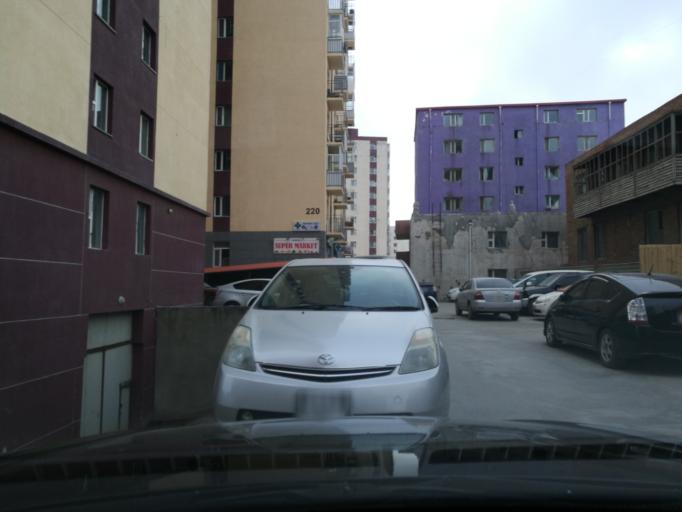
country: MN
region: Ulaanbaatar
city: Ulaanbaatar
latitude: 47.9308
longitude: 106.9144
